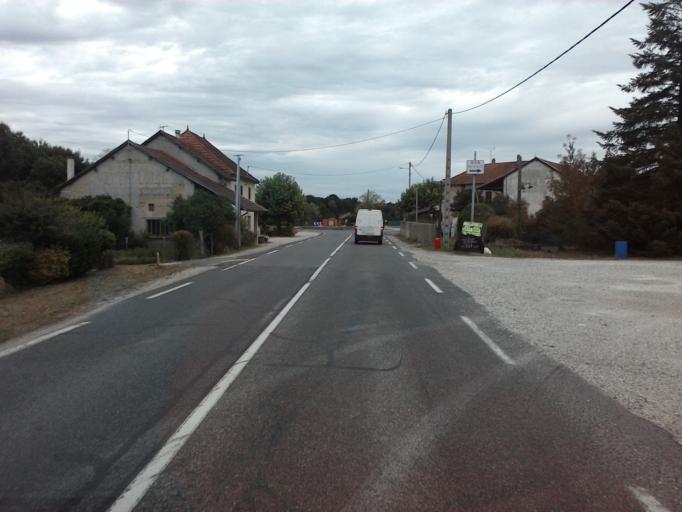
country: FR
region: Rhone-Alpes
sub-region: Departement de l'Isere
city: Sermerieu
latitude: 45.7175
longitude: 5.4233
